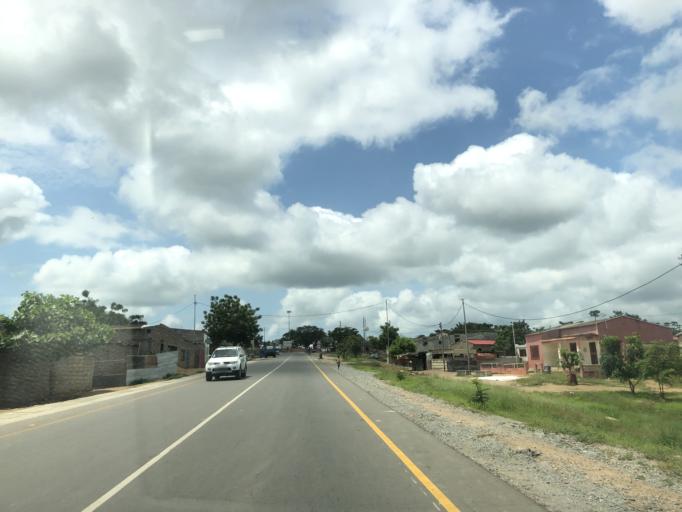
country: AO
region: Cuanza Norte
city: N'dalatando
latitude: -9.6816
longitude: 14.4738
